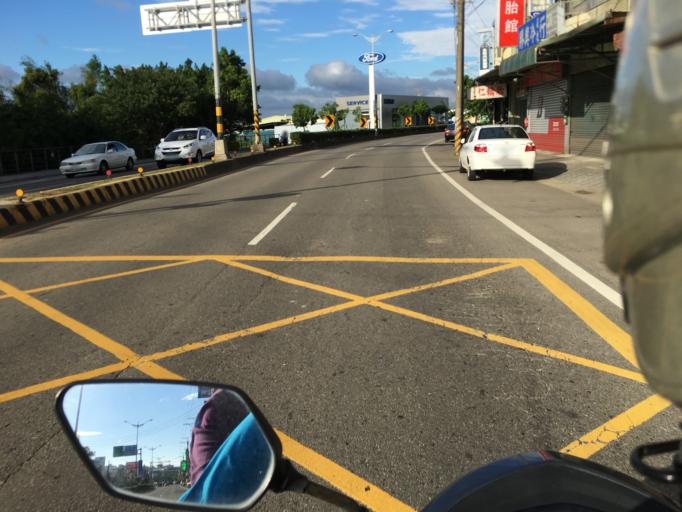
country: TW
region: Taiwan
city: Daxi
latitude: 24.8668
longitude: 121.2107
